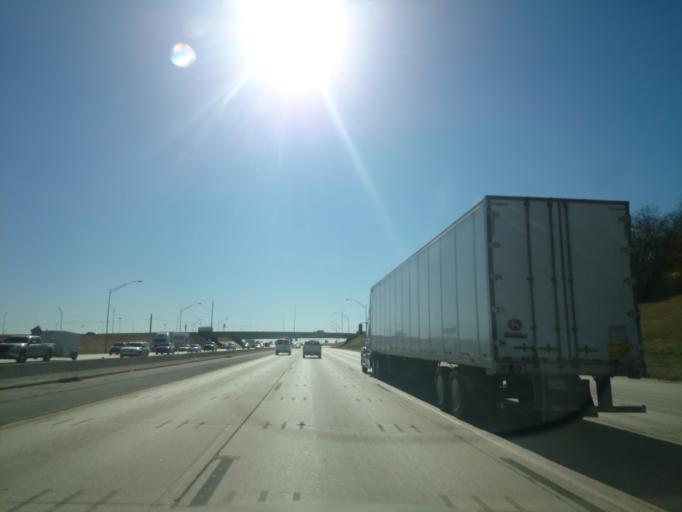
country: US
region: Oklahoma
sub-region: Oklahoma County
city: Warr Acres
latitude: 35.4812
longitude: -97.5786
